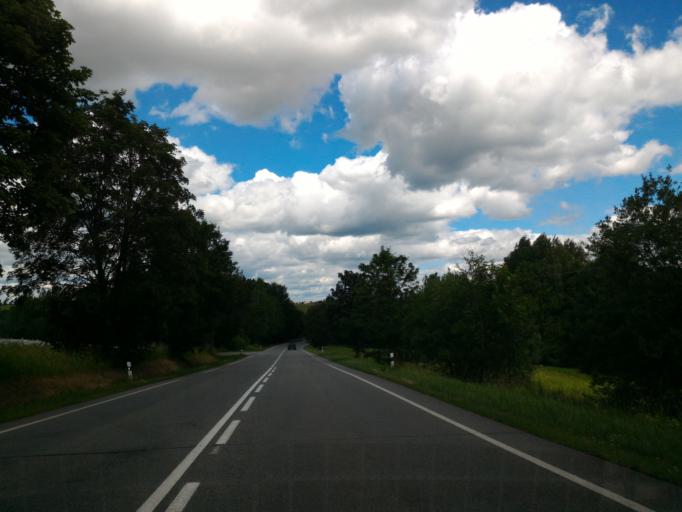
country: CZ
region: Vysocina
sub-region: Okres Jihlava
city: Trest'
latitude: 49.2583
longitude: 15.4718
